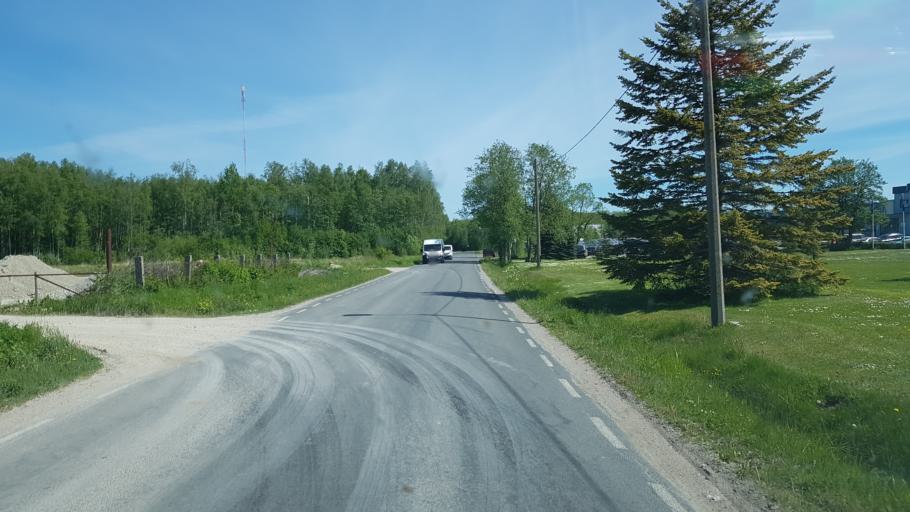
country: EE
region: Saare
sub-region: Kuressaare linn
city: Kuressaare
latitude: 58.2712
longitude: 22.4935
